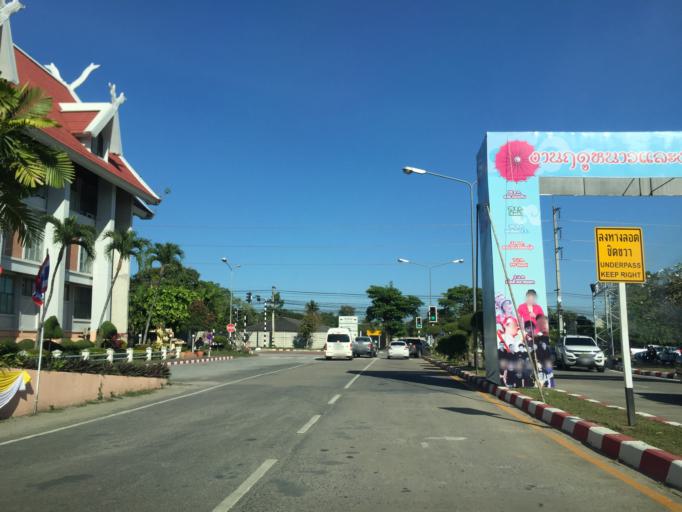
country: TH
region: Chiang Mai
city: Chiang Mai
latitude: 18.8413
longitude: 98.9712
